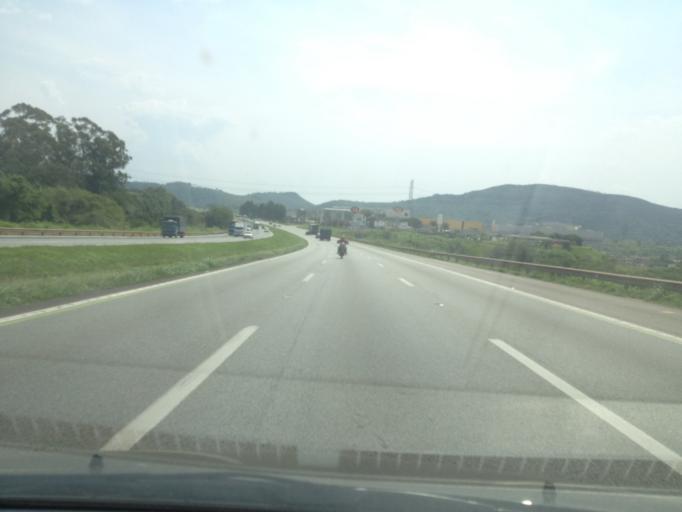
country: BR
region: Sao Paulo
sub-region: Pirapora Do Bom Jesus
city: Pirapora do Bom Jesus
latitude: -23.4361
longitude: -47.0923
